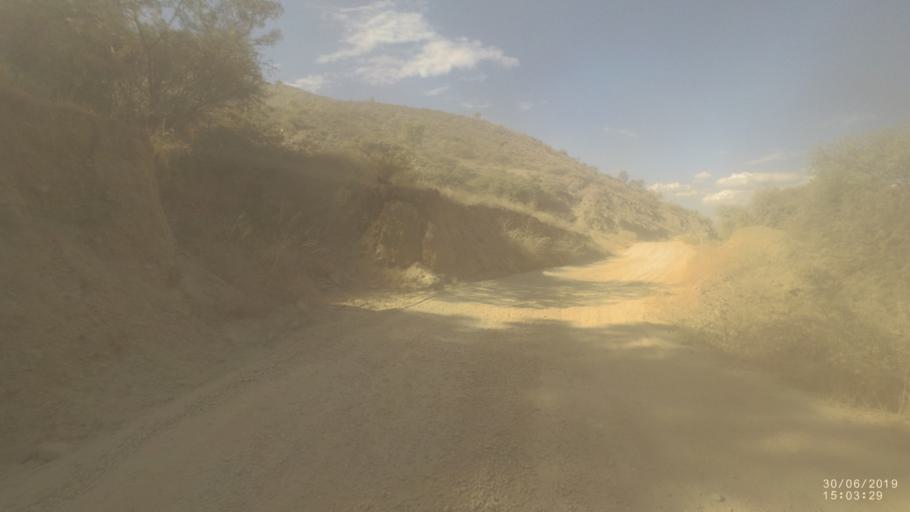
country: BO
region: Cochabamba
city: Irpa Irpa
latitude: -17.7313
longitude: -66.3268
